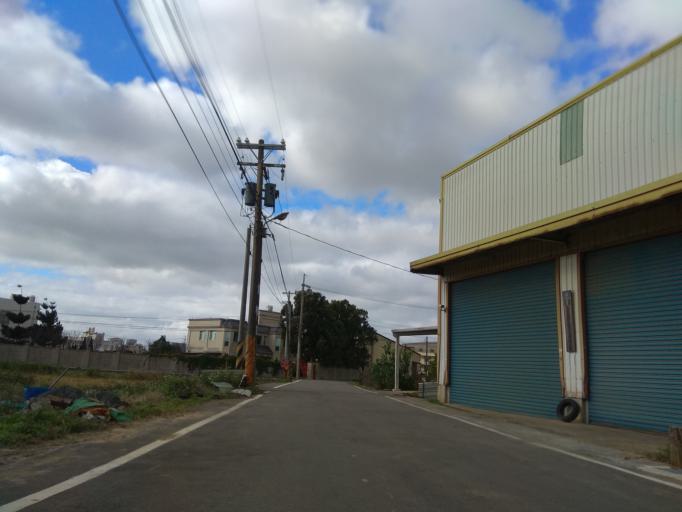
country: TW
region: Taiwan
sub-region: Hsinchu
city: Zhubei
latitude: 24.9748
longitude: 121.0836
